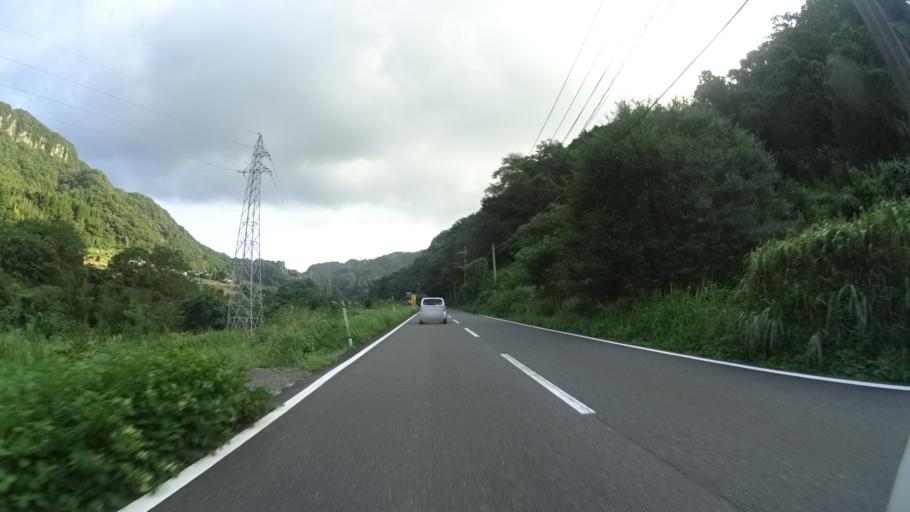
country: JP
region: Oita
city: Beppu
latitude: 33.3652
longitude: 131.3963
